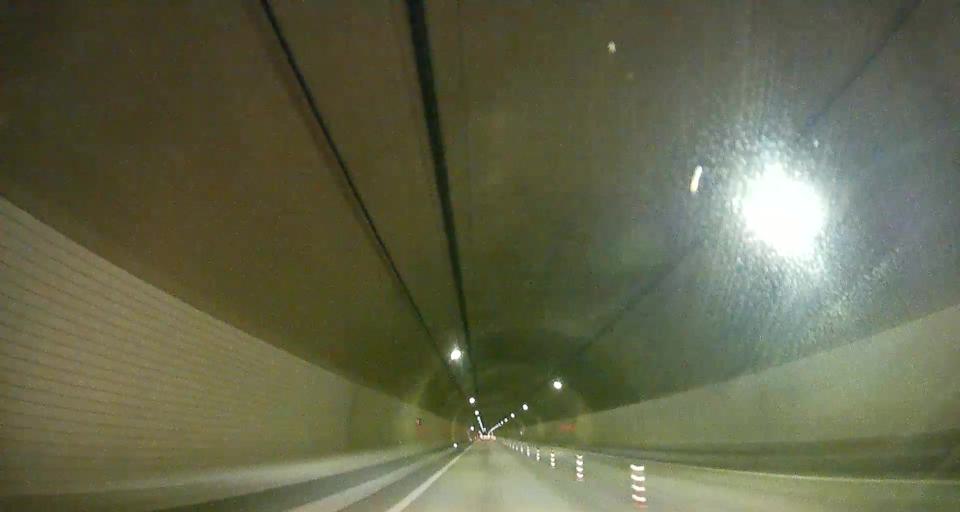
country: JP
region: Iwate
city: Miyako
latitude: 39.9294
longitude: 141.8689
